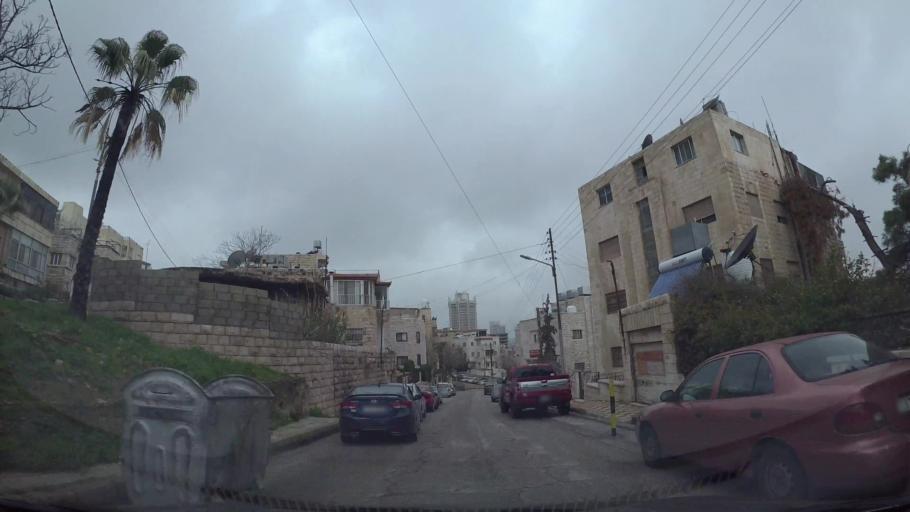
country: JO
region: Amman
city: Amman
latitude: 31.9525
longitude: 35.9200
